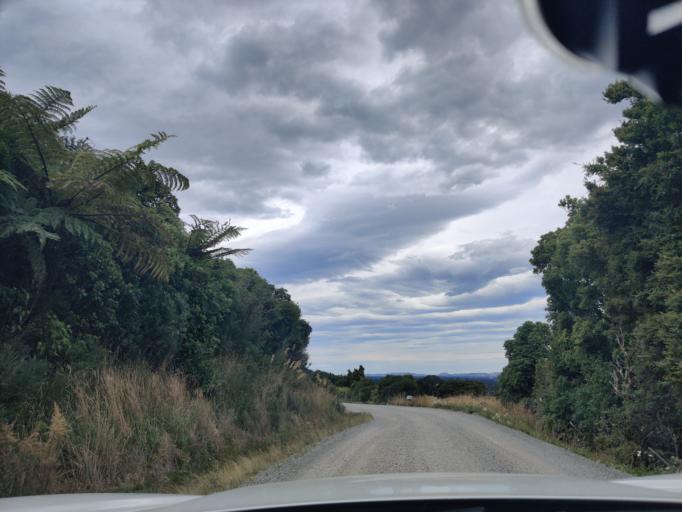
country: NZ
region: Wellington
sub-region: Masterton District
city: Masterton
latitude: -41.0391
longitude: 175.4138
